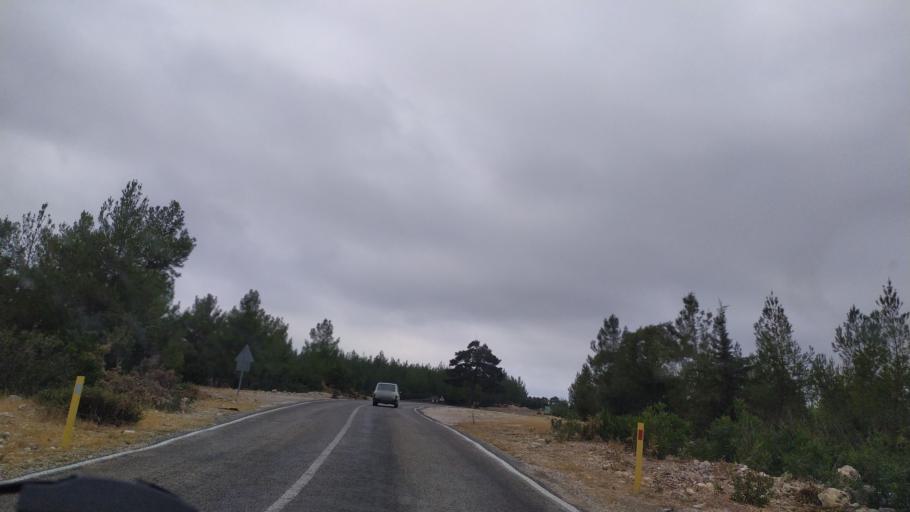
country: TR
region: Mersin
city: Silifke
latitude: 36.5416
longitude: 33.9283
